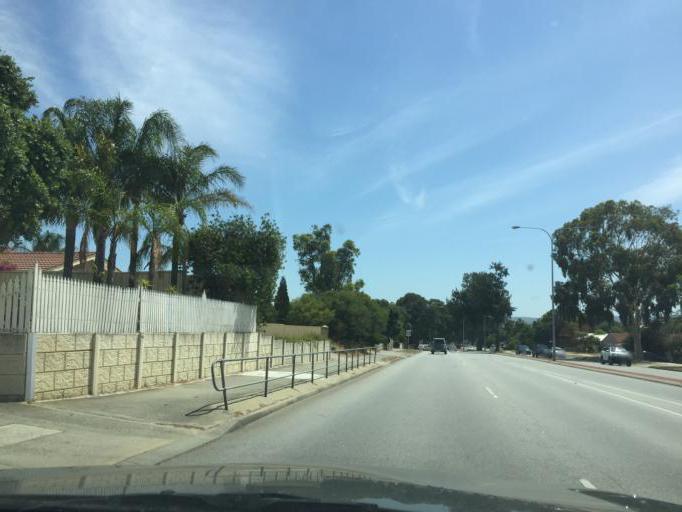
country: AU
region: Western Australia
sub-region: Gosnells
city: Thornlie
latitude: -32.0709
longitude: 115.9666
